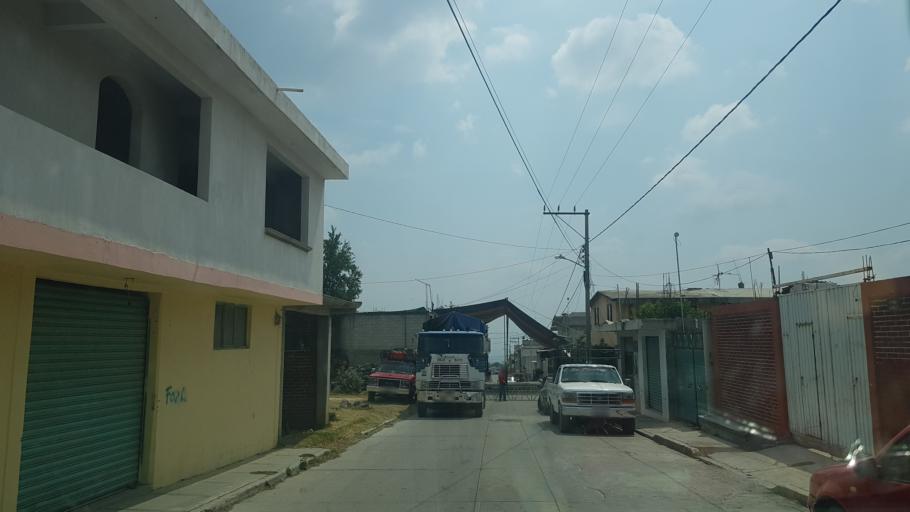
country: MX
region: Puebla
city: Domingo Arenas
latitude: 19.1359
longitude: -98.4928
